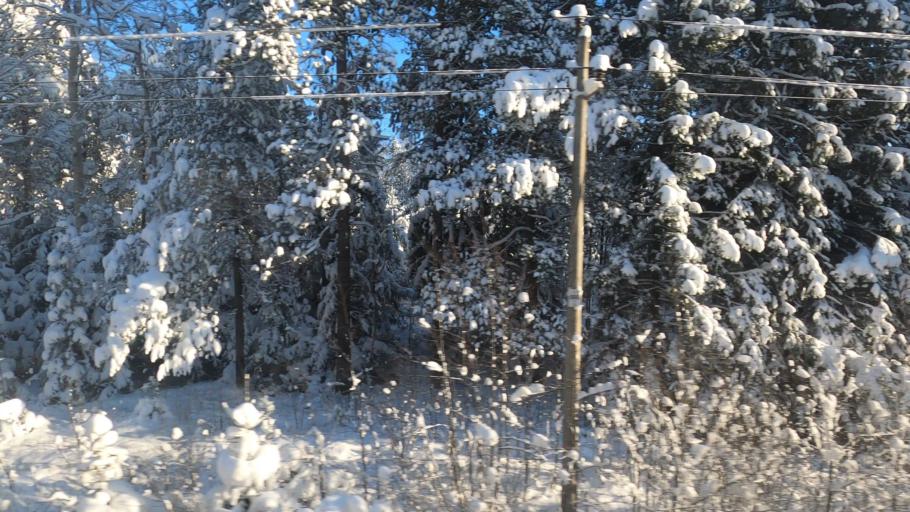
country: RU
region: Moskovskaya
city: Zhukovka
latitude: 56.4944
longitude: 37.5516
